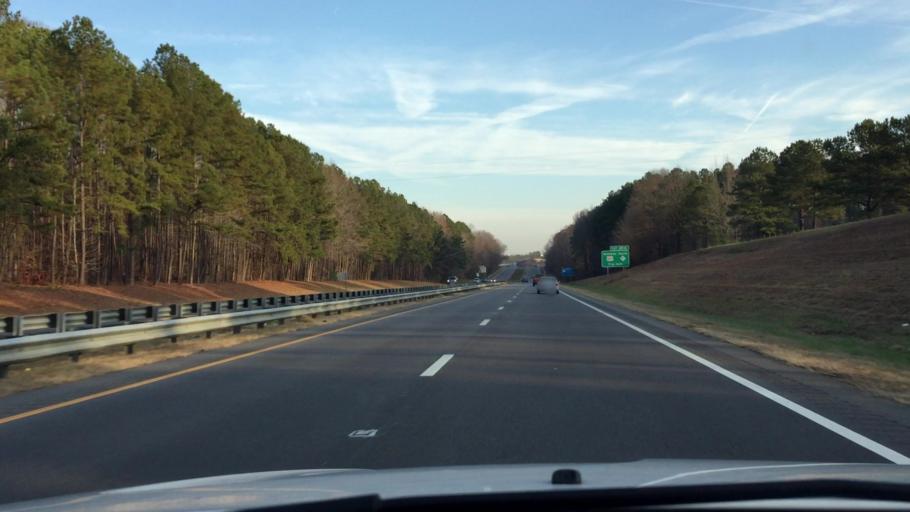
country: US
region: North Carolina
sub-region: Lee County
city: Sanford
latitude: 35.4744
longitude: -79.2010
